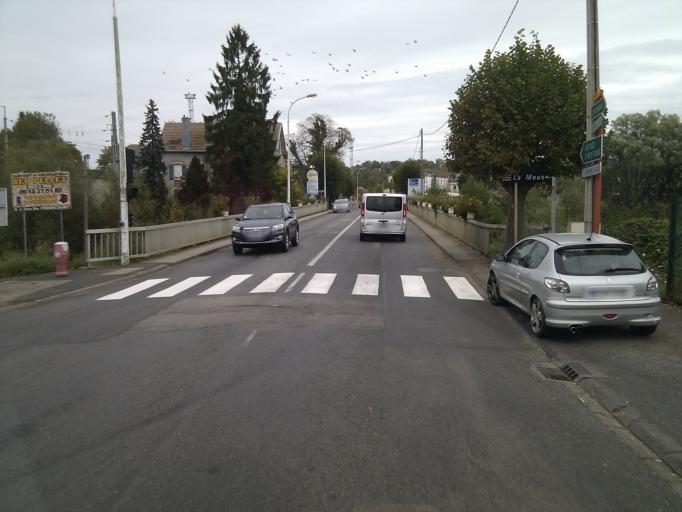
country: FR
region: Lorraine
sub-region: Departement des Vosges
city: Neufchateau
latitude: 48.3539
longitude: 5.6845
